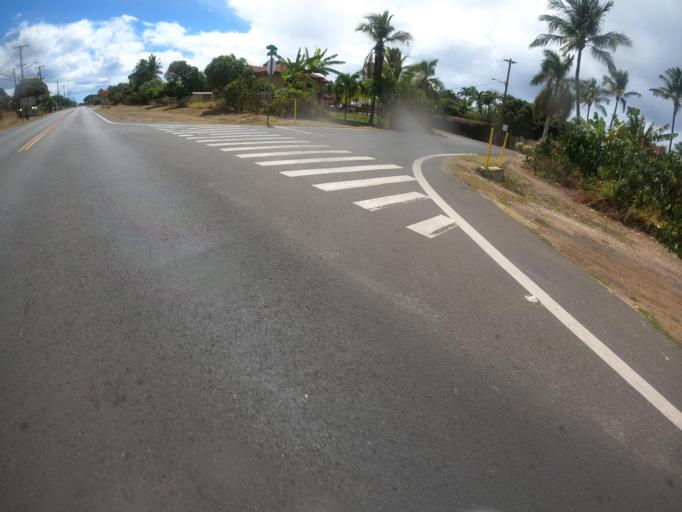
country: US
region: Hawaii
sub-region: Honolulu County
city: Makaha
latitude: 21.4745
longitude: -158.2185
